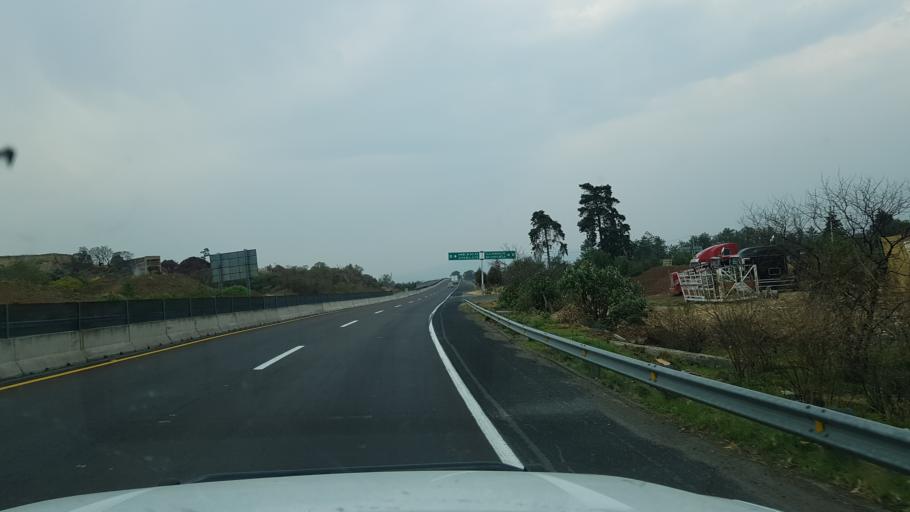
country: MX
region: Mexico
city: Miraflores
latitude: 19.2059
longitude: -98.8246
